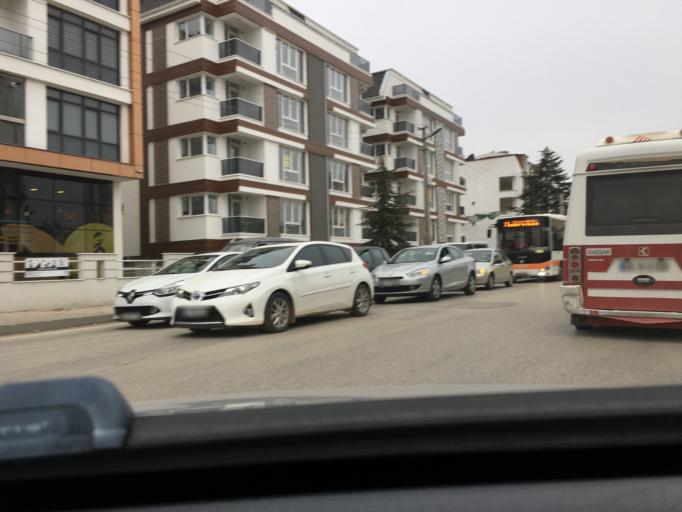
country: TR
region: Eskisehir
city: Eskisehir
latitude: 39.7702
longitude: 30.4784
